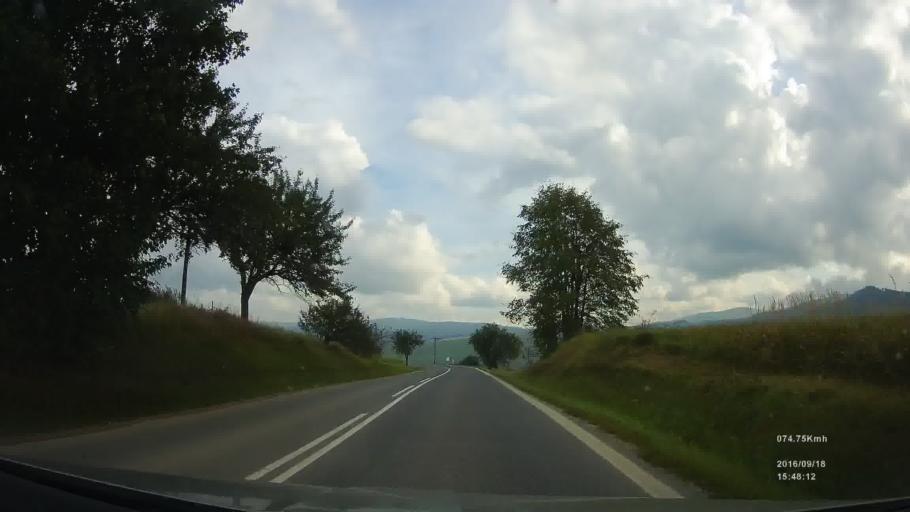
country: SK
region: Kosicky
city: Spisska Nova Ves
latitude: 48.9287
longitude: 20.5930
